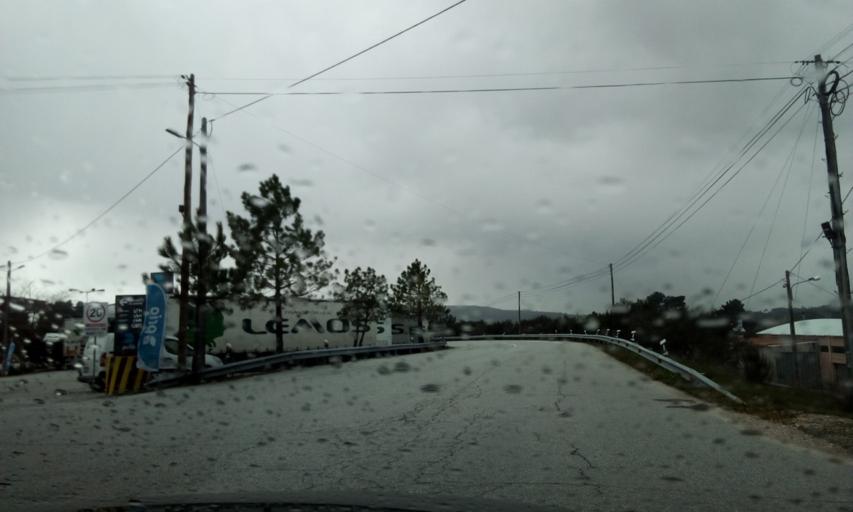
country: PT
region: Guarda
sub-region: Fornos de Algodres
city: Fornos de Algodres
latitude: 40.6190
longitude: -7.6135
